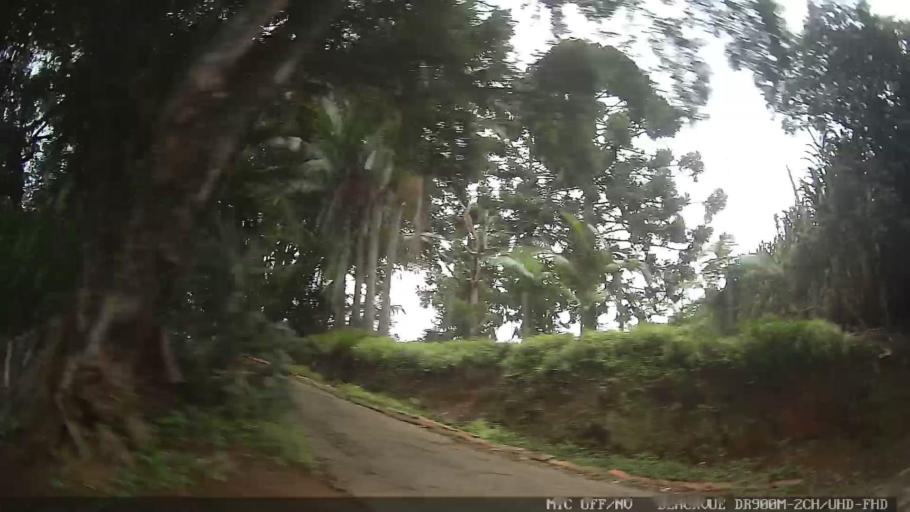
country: BR
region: Sao Paulo
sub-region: Biritiba-Mirim
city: Biritiba Mirim
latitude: -23.5411
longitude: -46.0945
